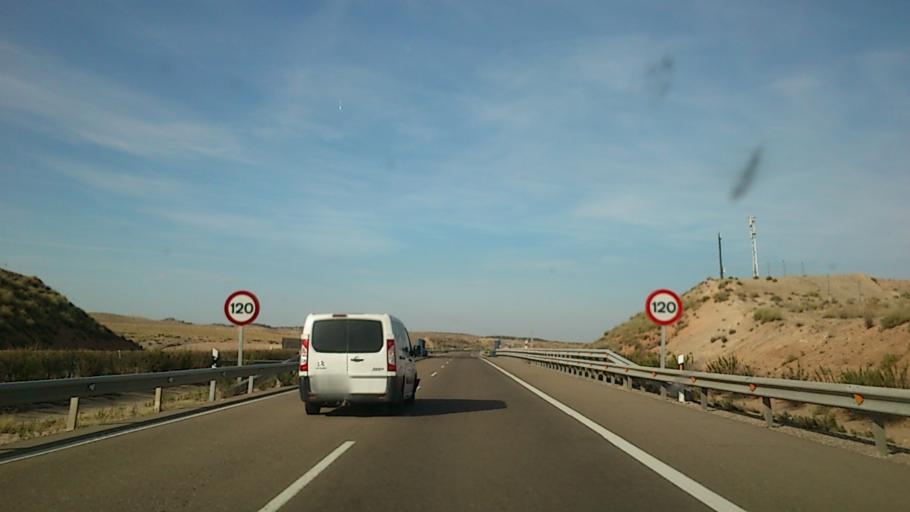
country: ES
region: Aragon
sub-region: Provincia de Zaragoza
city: Maria de Huerva
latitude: 41.5375
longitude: -1.0077
